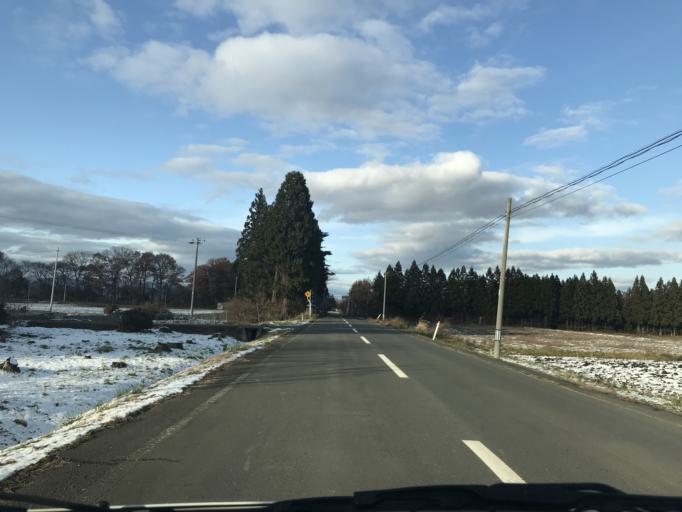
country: JP
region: Iwate
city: Kitakami
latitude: 39.2506
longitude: 141.0325
